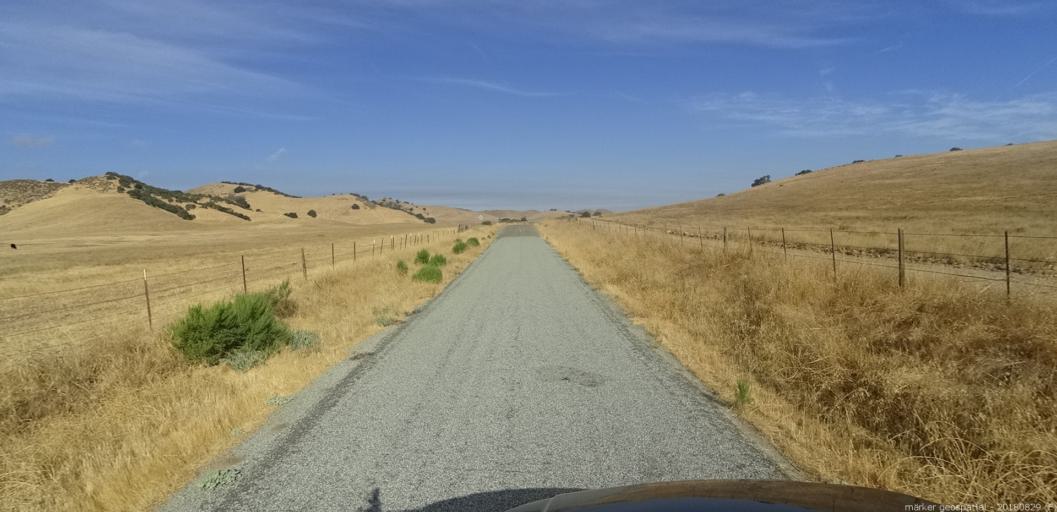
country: US
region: California
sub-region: Monterey County
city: King City
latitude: 36.0288
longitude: -120.9579
